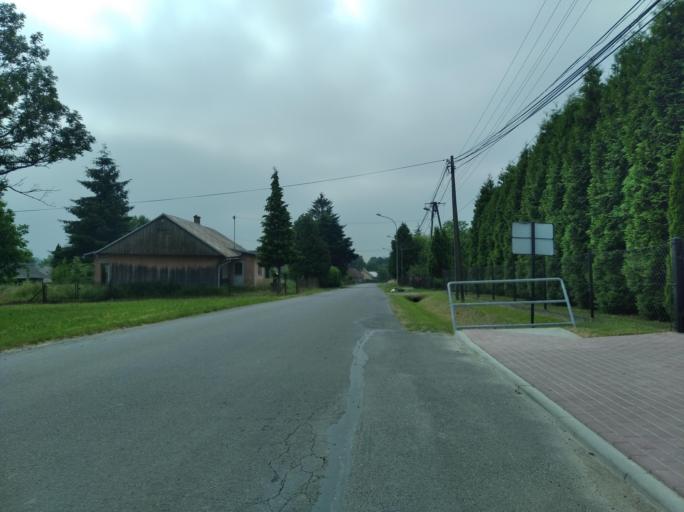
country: PL
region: Subcarpathian Voivodeship
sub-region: Powiat brzozowski
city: Haczow
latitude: 49.6600
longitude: 21.9002
